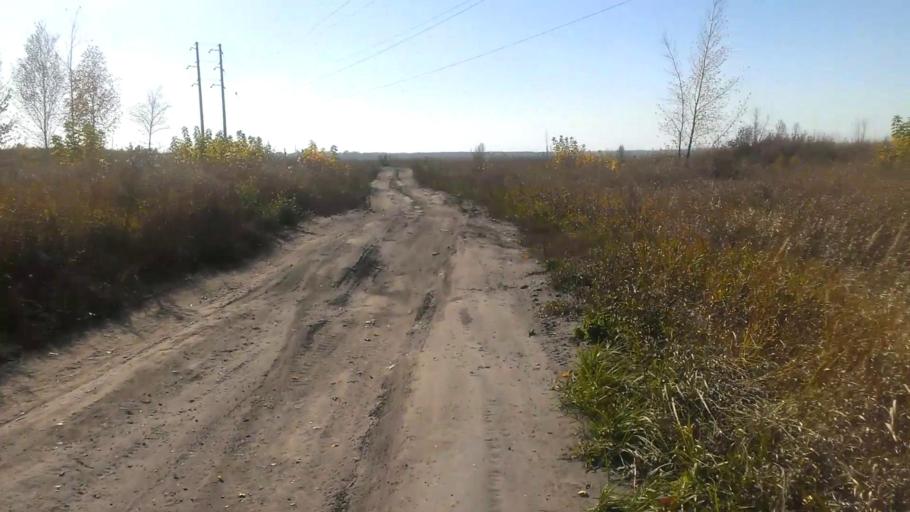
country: RU
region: Altai Krai
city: Novoaltaysk
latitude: 53.3670
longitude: 83.9459
